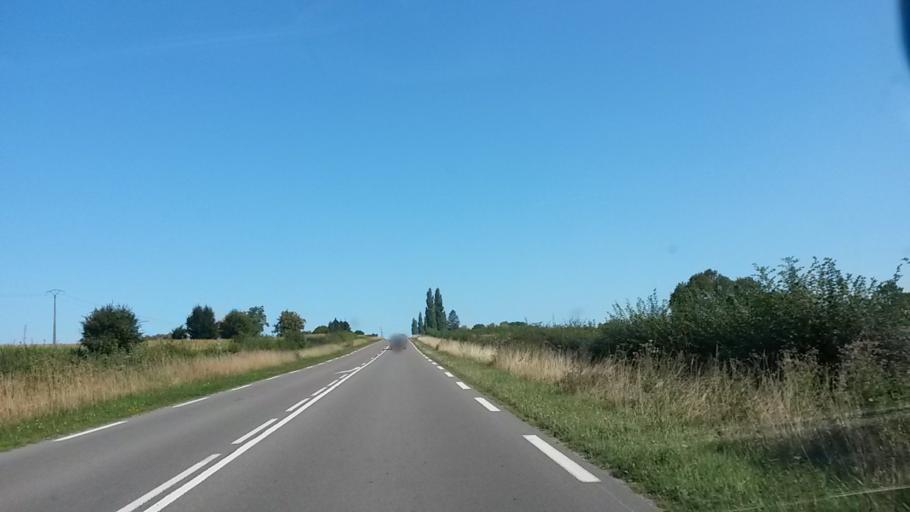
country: FR
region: Nord-Pas-de-Calais
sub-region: Departement du Nord
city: Avesnes-sur-Helpe
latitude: 50.0809
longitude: 3.9296
